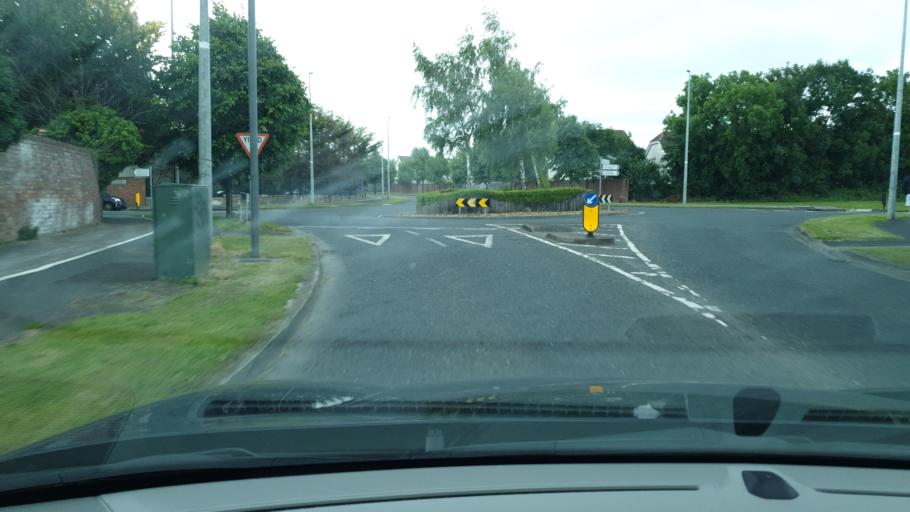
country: IE
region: Leinster
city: Lucan
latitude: 53.3396
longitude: -6.4401
